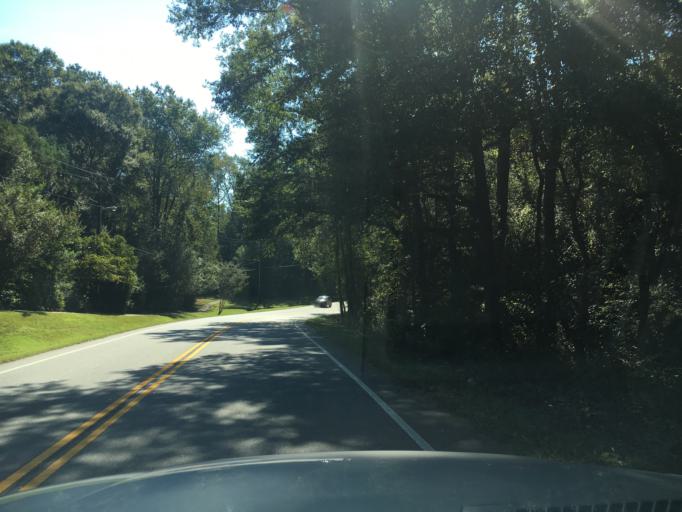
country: US
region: South Carolina
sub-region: Greenville County
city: Taylors
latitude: 34.8849
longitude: -82.2843
